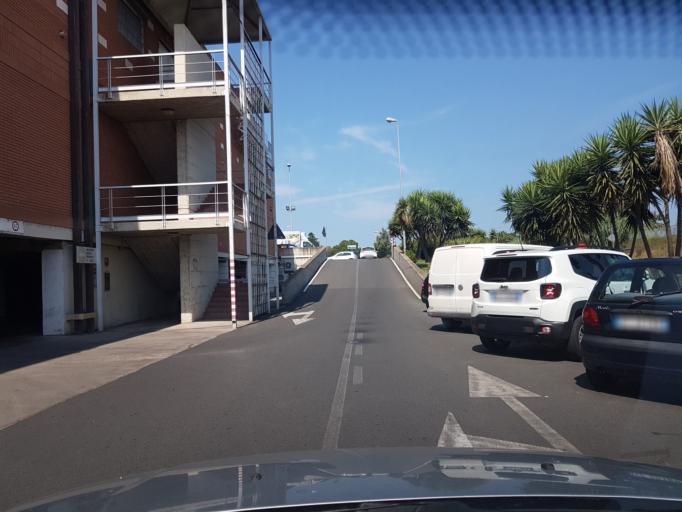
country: IT
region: Sardinia
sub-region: Provincia di Oristano
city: Oristano
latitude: 39.9162
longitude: 8.5864
